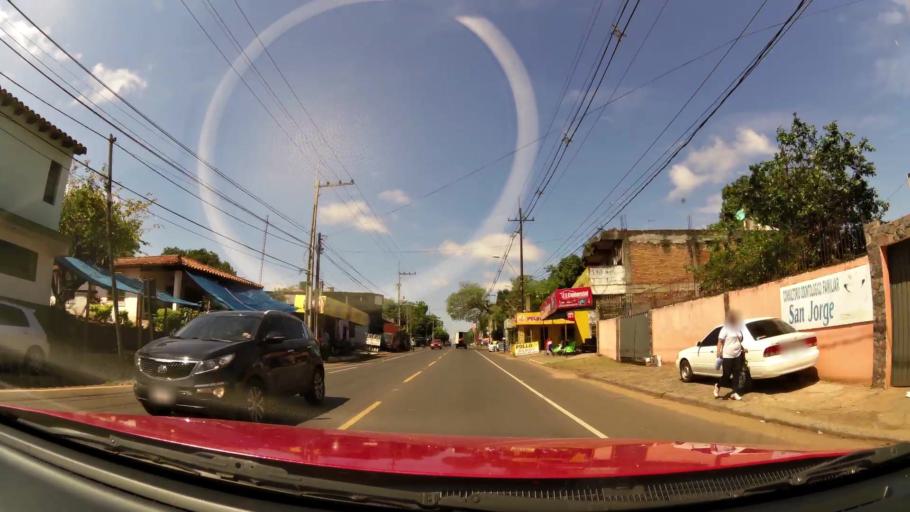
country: PY
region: Central
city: San Lorenzo
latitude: -25.3115
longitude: -57.5062
